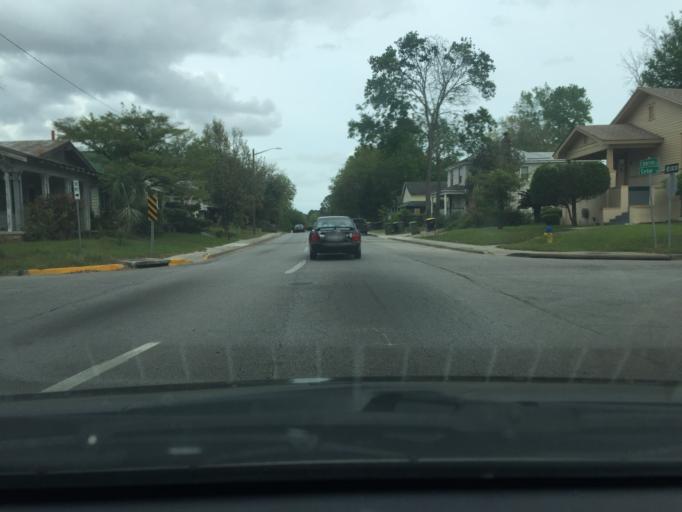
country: US
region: Georgia
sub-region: Chatham County
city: Savannah
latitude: 32.0572
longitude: -81.0784
